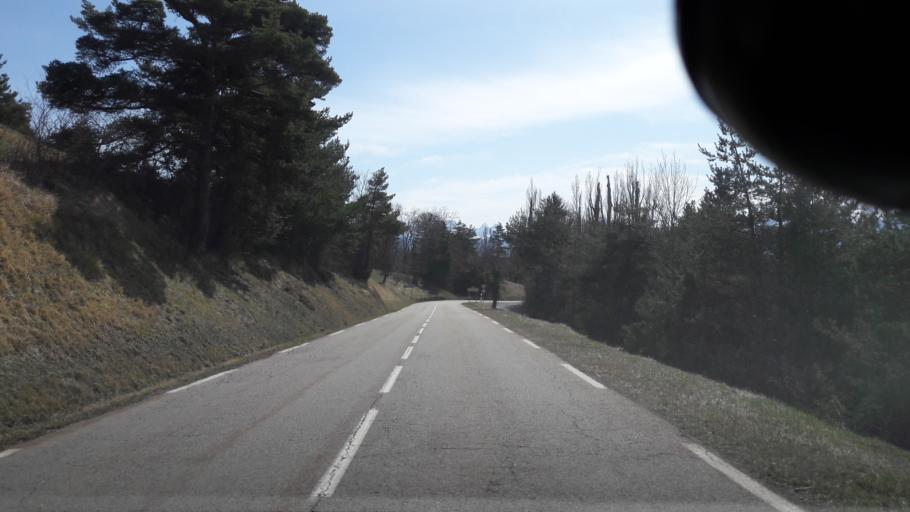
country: FR
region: Rhone-Alpes
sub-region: Departement de l'Isere
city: La Motte-Saint-Martin
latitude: 44.8885
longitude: 5.6377
